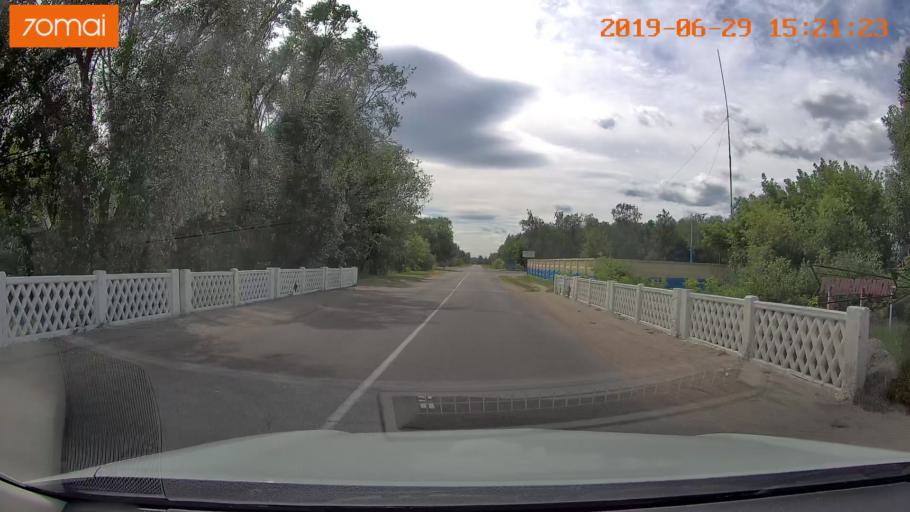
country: BY
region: Brest
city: Mikashevichy
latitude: 52.2147
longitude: 27.4627
